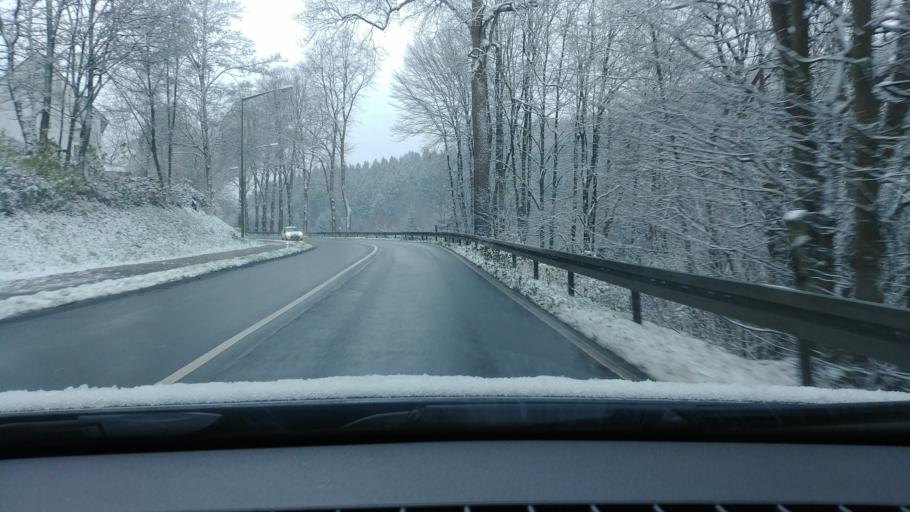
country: DE
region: North Rhine-Westphalia
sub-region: Regierungsbezirk Koln
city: Gummersbach
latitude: 50.9962
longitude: 7.5696
